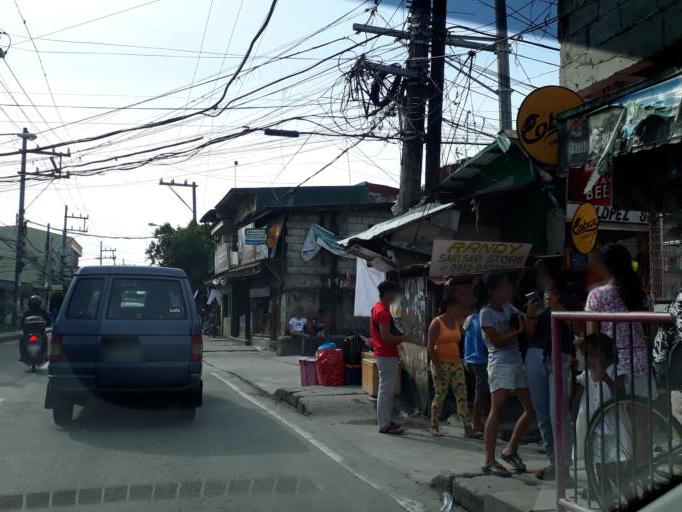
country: PH
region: Metro Manila
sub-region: Caloocan City
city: Niugan
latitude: 14.6691
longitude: 120.9620
